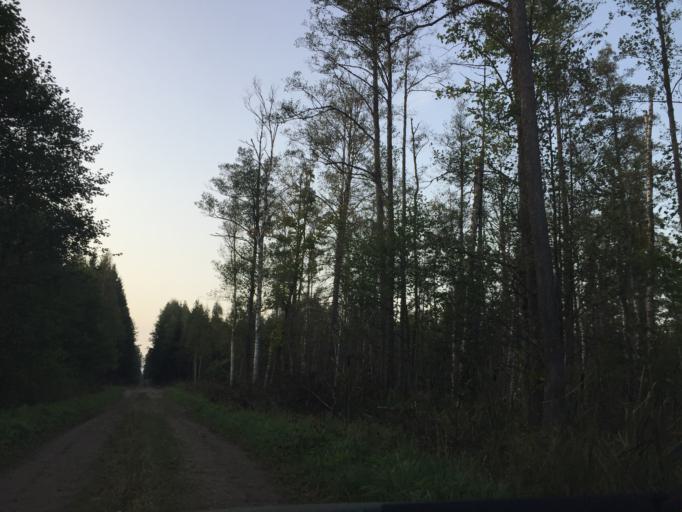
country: LV
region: Ikskile
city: Ikskile
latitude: 56.9335
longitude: 24.4834
